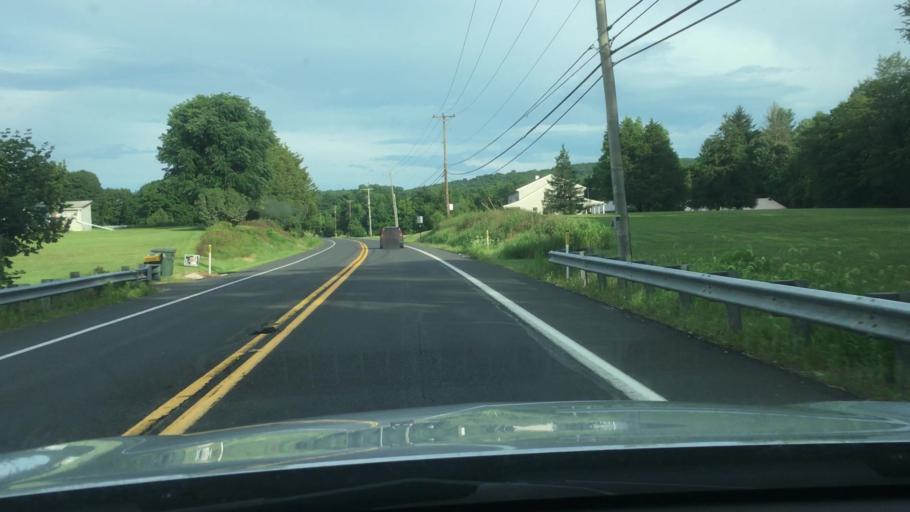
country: US
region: Pennsylvania
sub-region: York County
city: Dover
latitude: 40.0415
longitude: -76.8943
